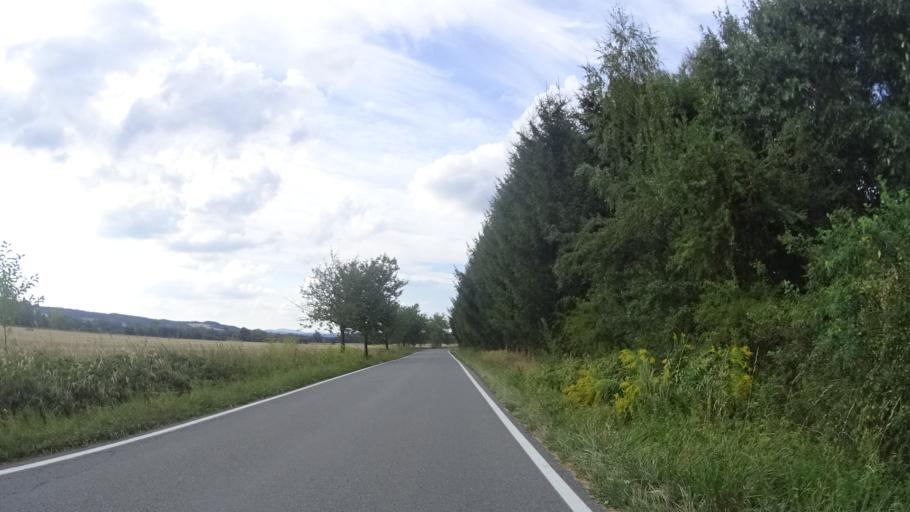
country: CZ
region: Olomoucky
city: Dubicko
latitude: 49.8216
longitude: 16.9370
